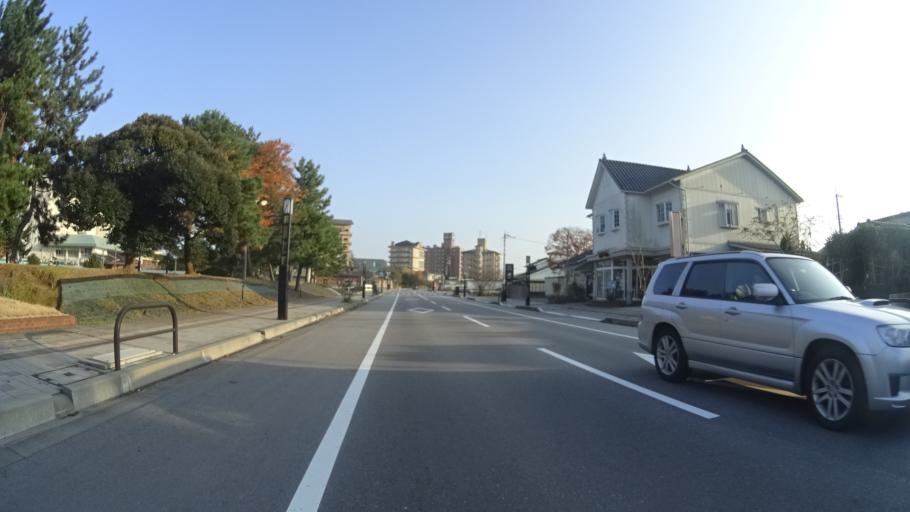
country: JP
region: Ishikawa
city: Nanao
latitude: 37.0868
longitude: 136.9238
